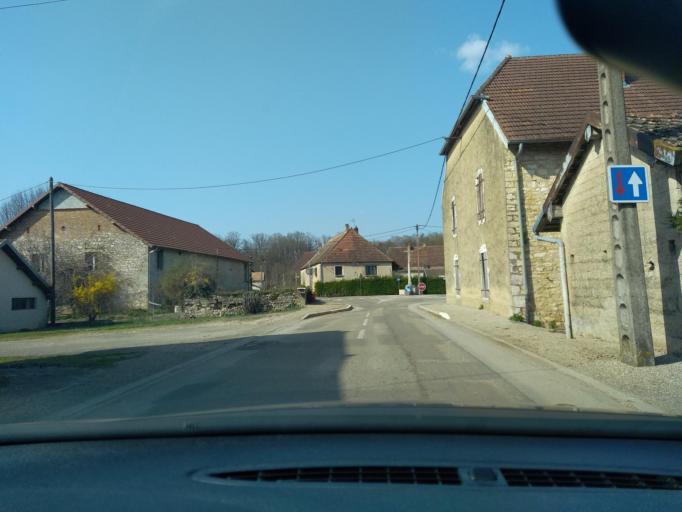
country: FR
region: Franche-Comte
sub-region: Departement du Jura
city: Mont-sous-Vaudrey
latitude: 47.0149
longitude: 5.5936
